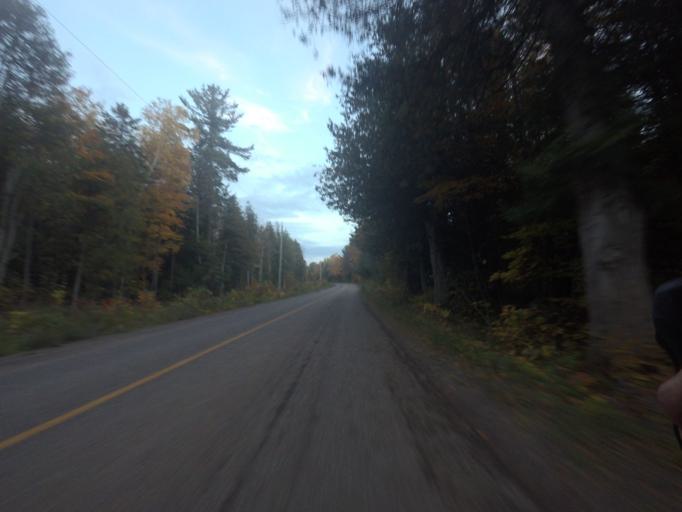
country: CA
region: Ontario
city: Renfrew
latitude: 45.3511
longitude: -76.9486
